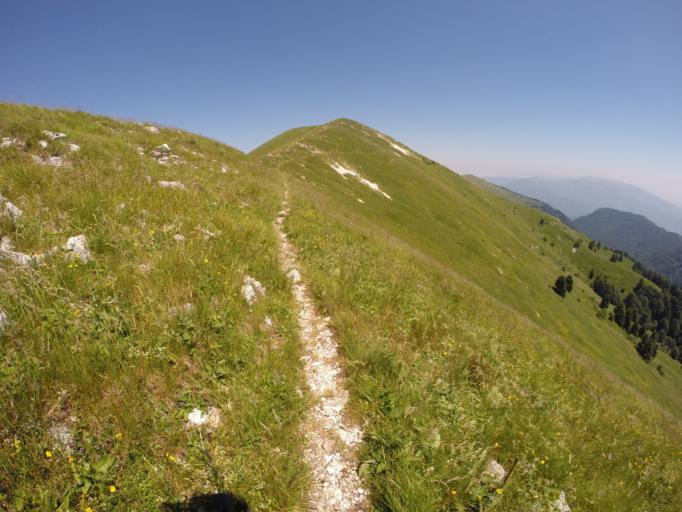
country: IT
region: Veneto
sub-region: Provincia di Treviso
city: Crespano del Grappa
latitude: 45.9054
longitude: 11.8232
